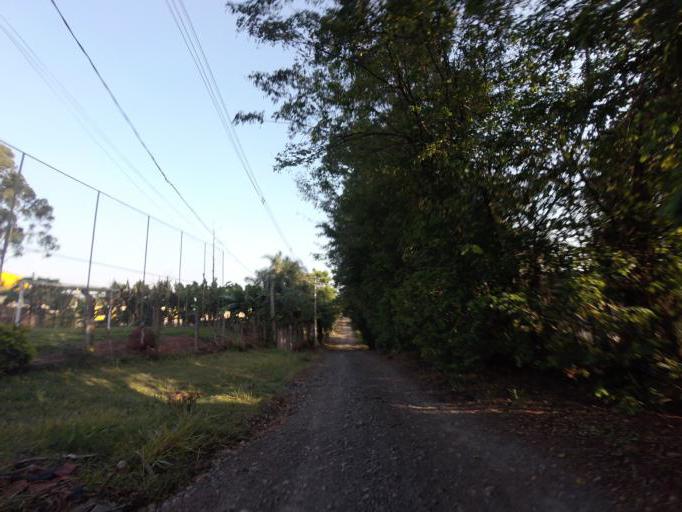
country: BR
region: Sao Paulo
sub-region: Piracicaba
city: Piracicaba
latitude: -22.7479
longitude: -47.6048
